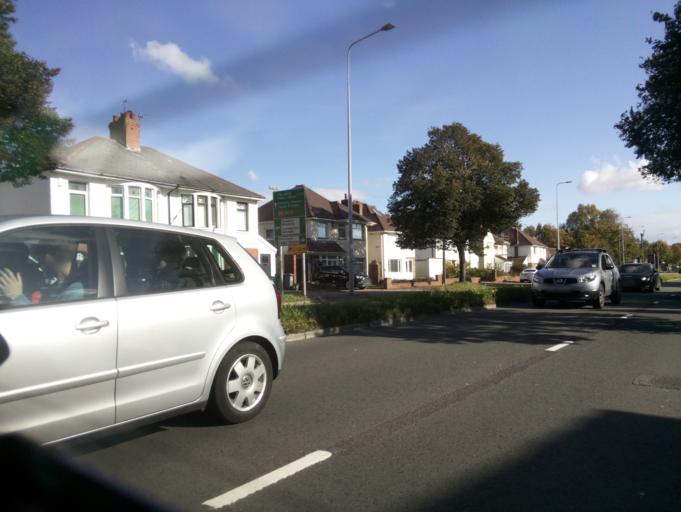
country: GB
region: Wales
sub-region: Cardiff
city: Radyr
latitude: 51.5178
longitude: -3.2187
